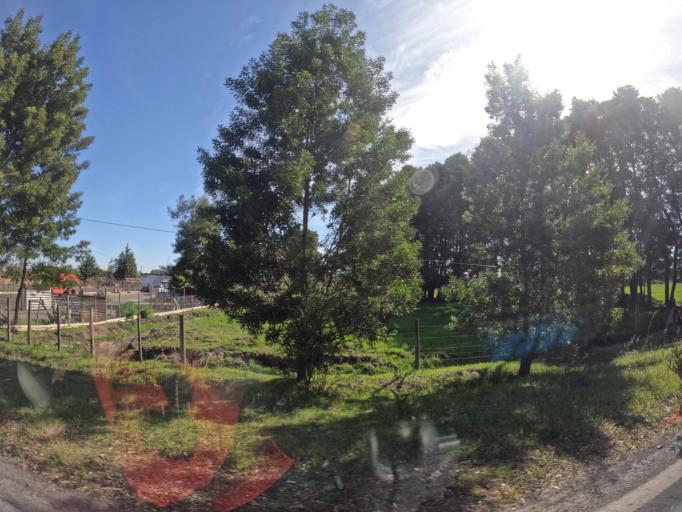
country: CL
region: Biobio
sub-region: Provincia de Biobio
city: Cabrero
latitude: -37.0367
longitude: -72.3727
